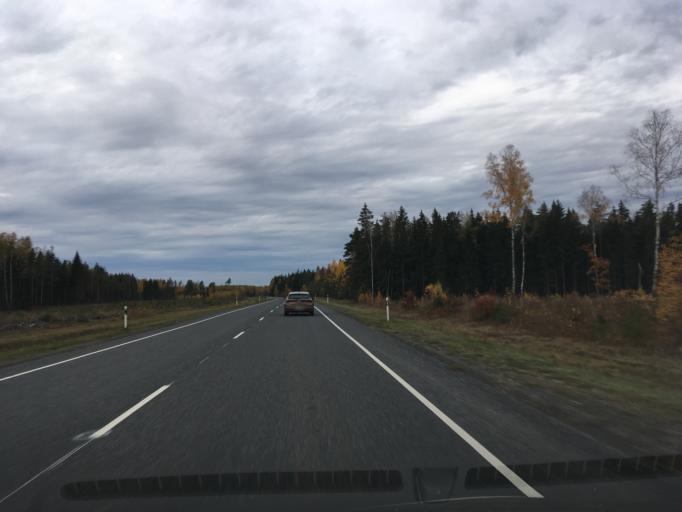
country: EE
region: Harju
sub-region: Nissi vald
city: Turba
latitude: 58.9646
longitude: 24.0703
